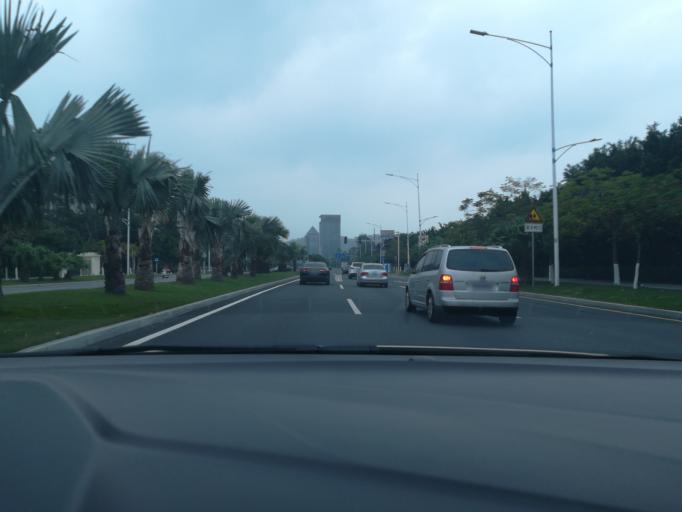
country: CN
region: Guangdong
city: Nansha
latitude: 22.7802
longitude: 113.5947
